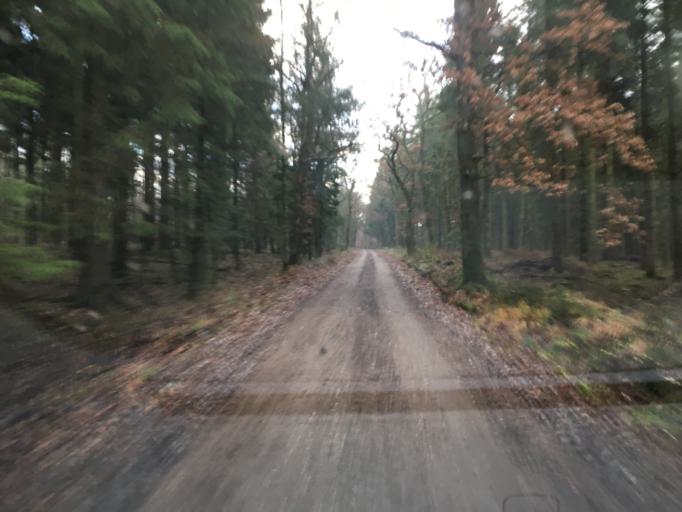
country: DK
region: South Denmark
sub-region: Tonder Kommune
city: Logumkloster
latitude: 55.1279
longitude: 8.8789
